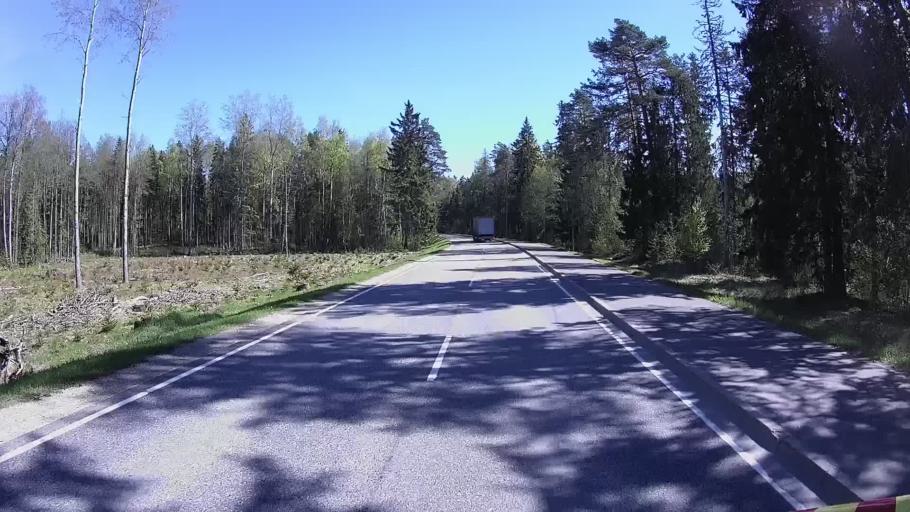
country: EE
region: Harju
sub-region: Kuusalu vald
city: Kuusalu
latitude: 59.2730
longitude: 25.6330
